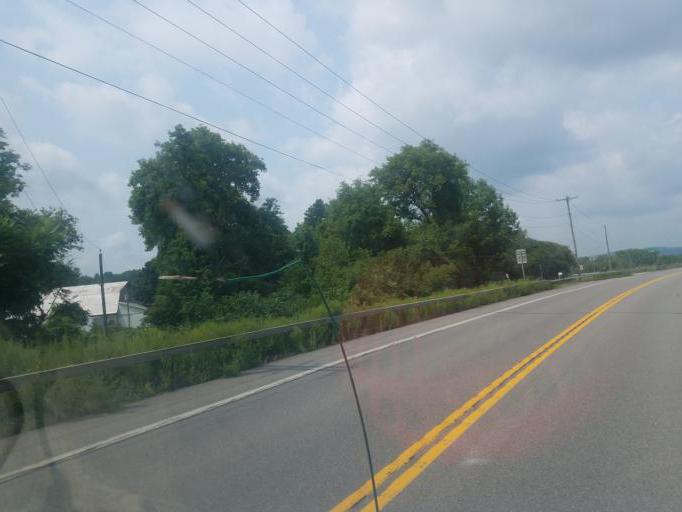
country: US
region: New York
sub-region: Herkimer County
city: Herkimer
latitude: 43.0135
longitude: -74.9464
